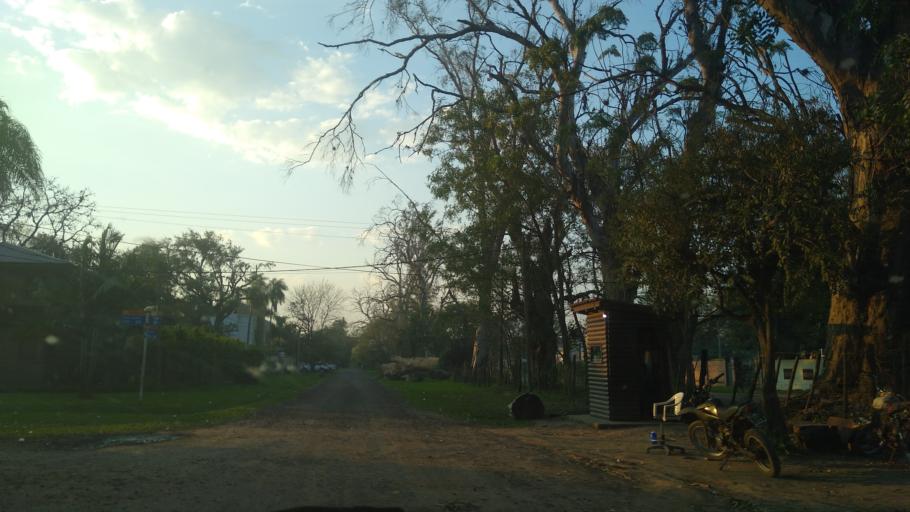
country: AR
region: Chaco
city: Barranqueras
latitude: -27.4671
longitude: -58.9576
